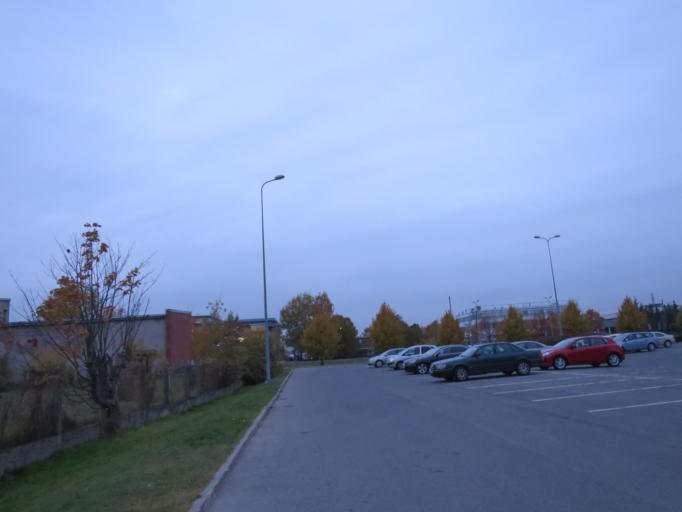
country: LV
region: Riga
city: Riga
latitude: 56.9681
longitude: 24.1199
